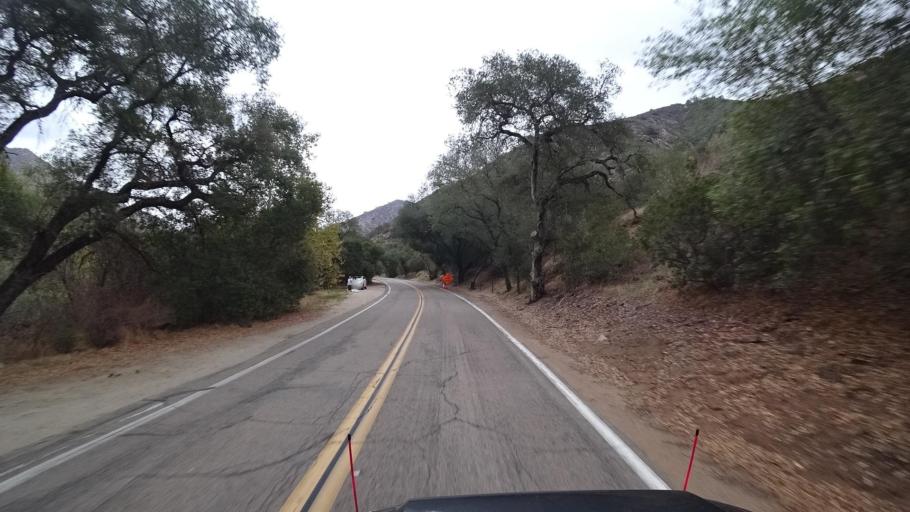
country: US
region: California
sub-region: San Diego County
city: Harbison Canyon
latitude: 32.8861
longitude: -116.8280
